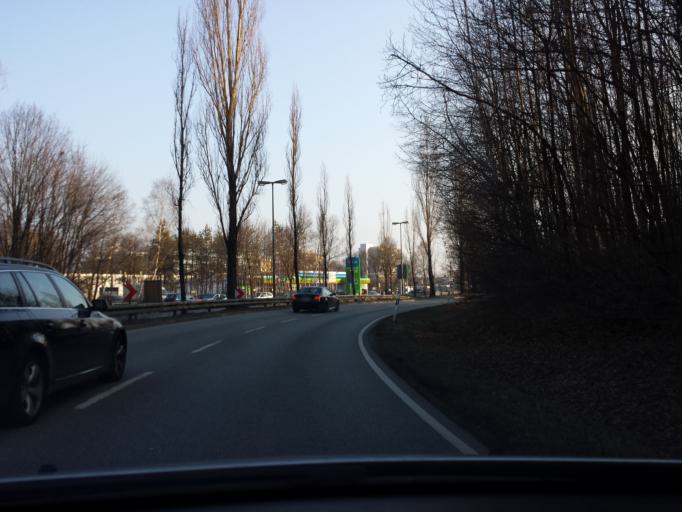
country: DE
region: Bavaria
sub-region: Upper Bavaria
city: Munich
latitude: 48.1887
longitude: 11.5298
